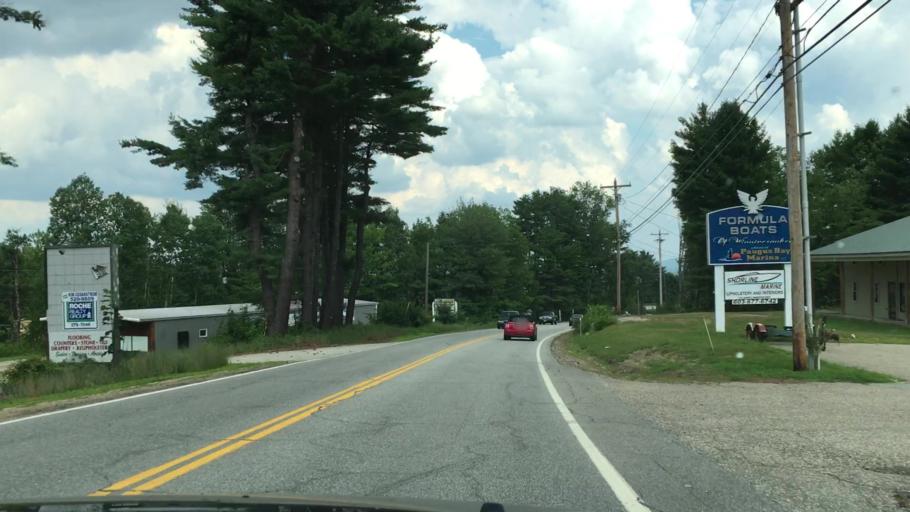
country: US
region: New Hampshire
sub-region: Belknap County
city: Meredith
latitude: 43.6371
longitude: -71.4925
